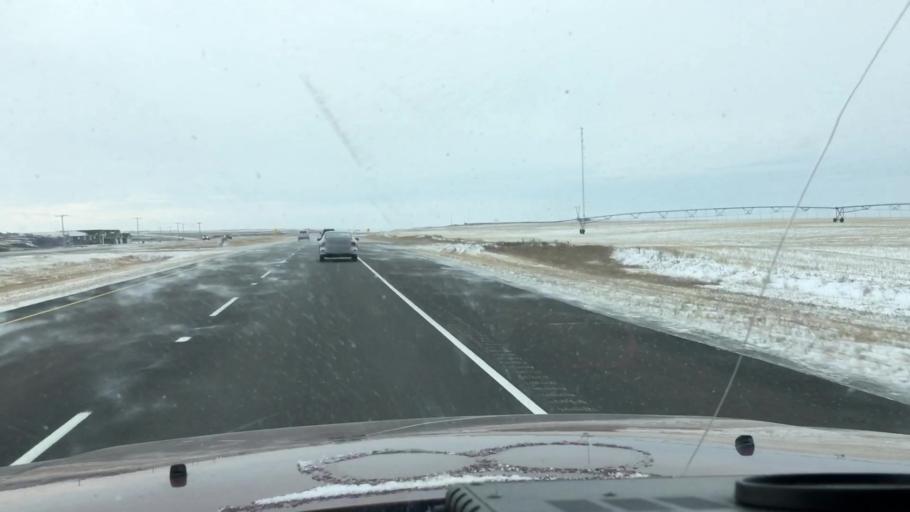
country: CA
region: Saskatchewan
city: Saskatoon
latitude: 51.7444
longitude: -106.4764
